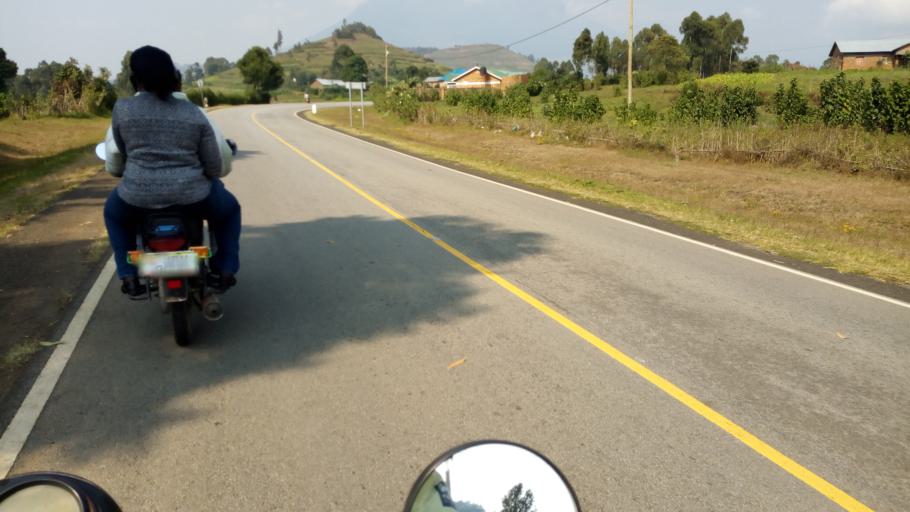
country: UG
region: Western Region
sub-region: Kisoro District
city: Kisoro
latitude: -1.3060
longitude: 29.7248
